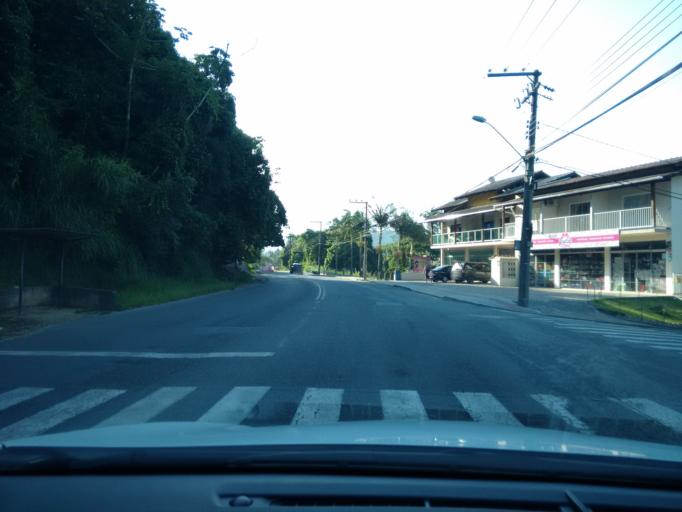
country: BR
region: Santa Catarina
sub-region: Blumenau
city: Blumenau
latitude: -26.8566
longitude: -49.1115
